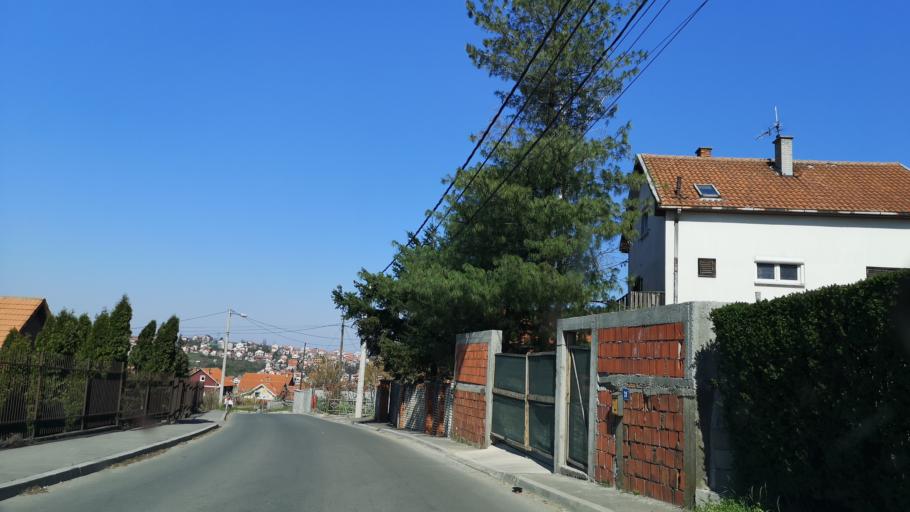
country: RS
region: Central Serbia
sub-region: Belgrade
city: Zvezdara
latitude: 44.7624
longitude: 20.5392
